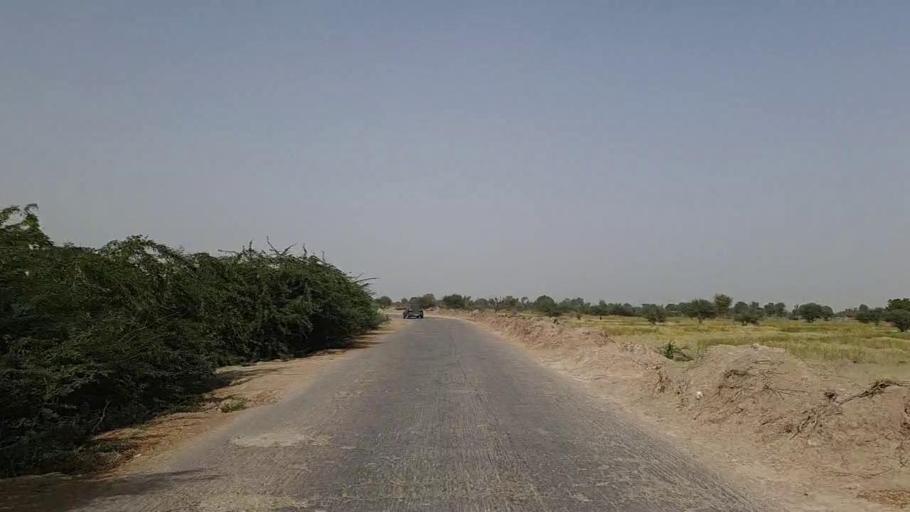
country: PK
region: Sindh
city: Tando Bago
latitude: 24.8931
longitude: 69.0780
